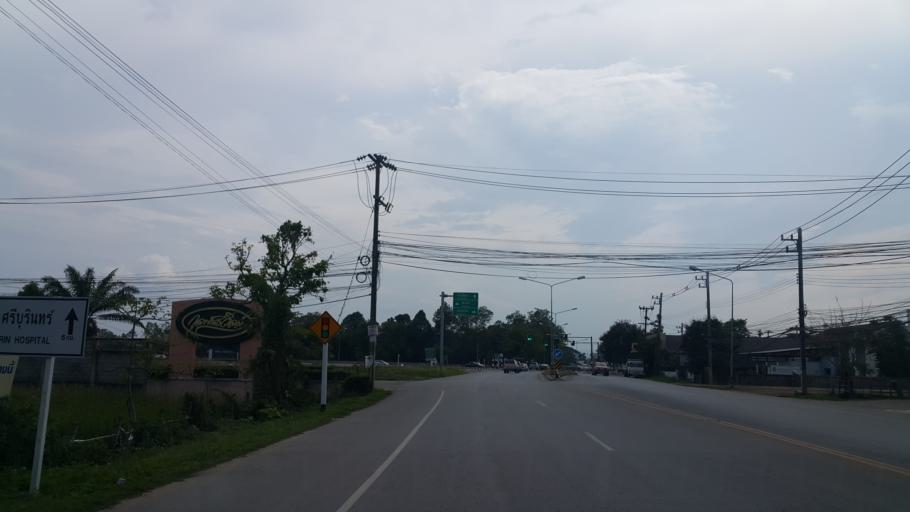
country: TH
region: Chiang Rai
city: Chiang Rai
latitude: 19.9097
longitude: 99.8609
